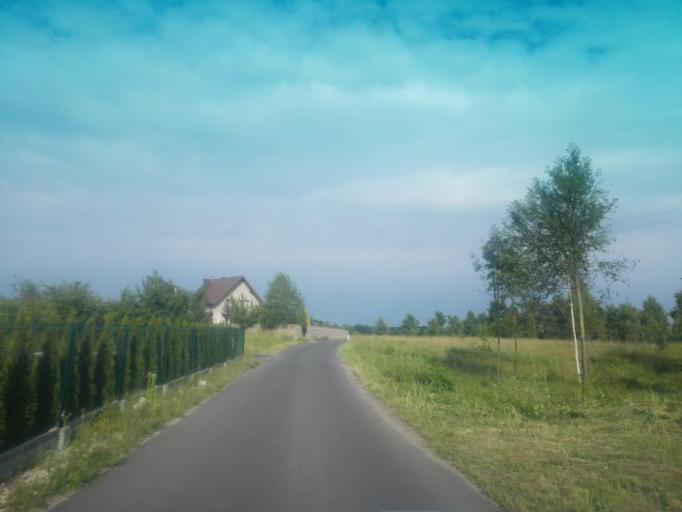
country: PL
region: Silesian Voivodeship
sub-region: Powiat czestochowski
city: Mstow
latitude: 50.8318
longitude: 19.3061
